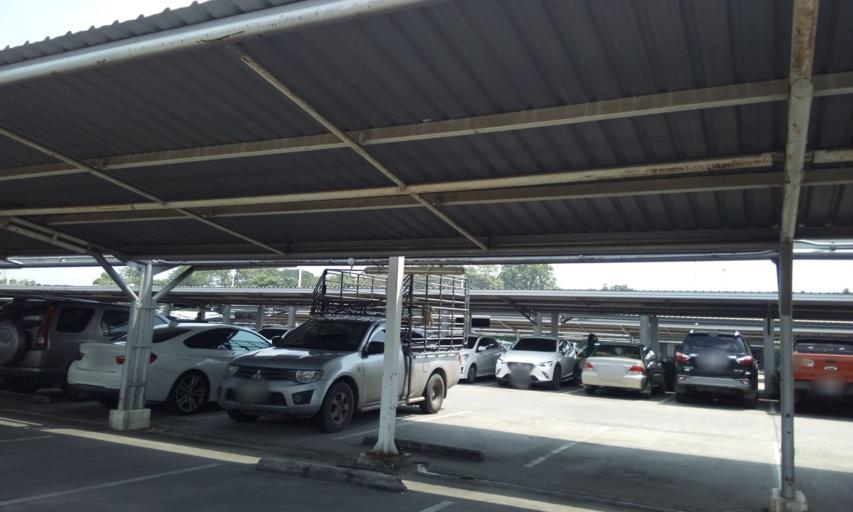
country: TH
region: Pathum Thani
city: Ban Rangsit
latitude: 14.0339
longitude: 100.7664
